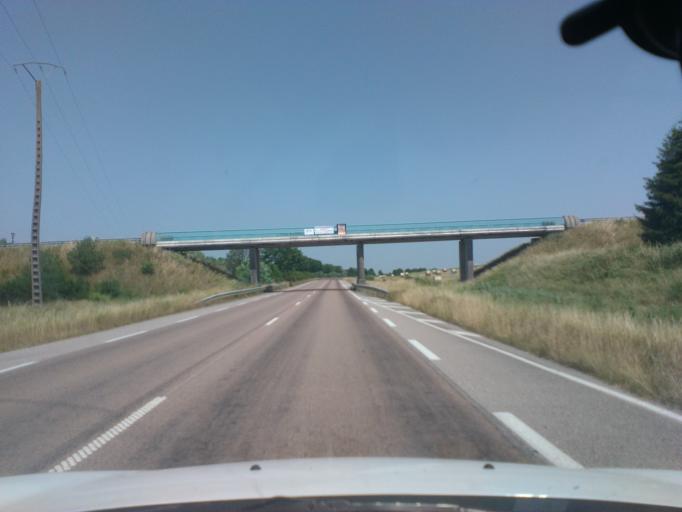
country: FR
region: Lorraine
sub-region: Departement des Vosges
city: Vittel
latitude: 48.3085
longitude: 5.9428
